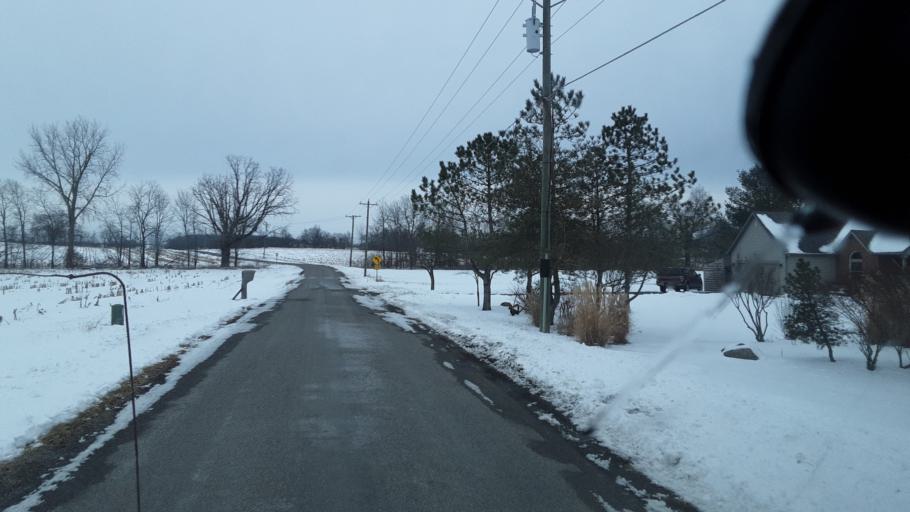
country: US
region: Ohio
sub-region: Madison County
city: Plain City
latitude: 40.1601
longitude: -83.3282
